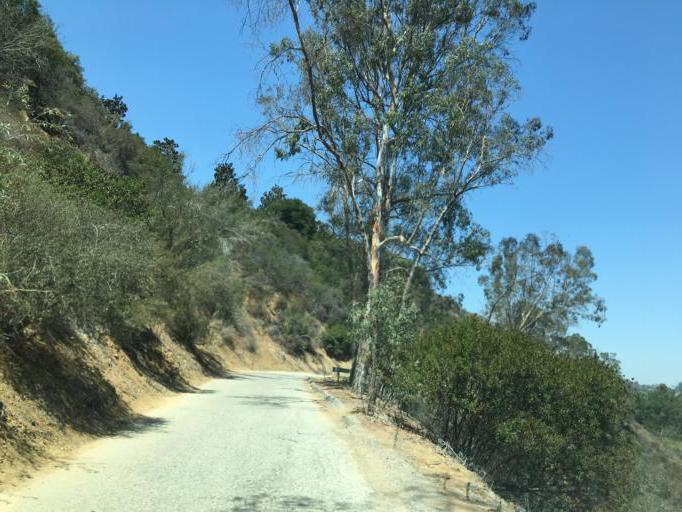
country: US
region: California
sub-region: Los Angeles County
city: Beverly Hills
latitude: 34.1125
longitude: -118.4161
